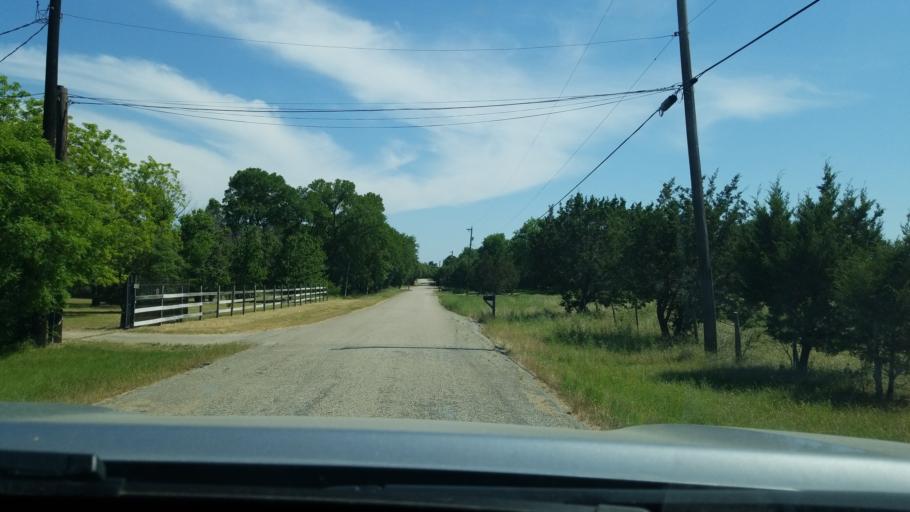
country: US
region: Texas
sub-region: Bexar County
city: Timberwood Park
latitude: 29.7522
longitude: -98.5179
